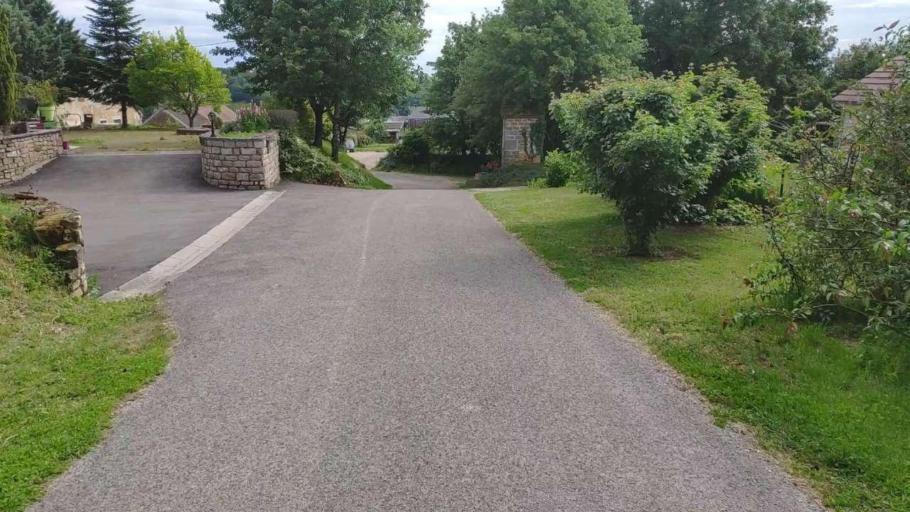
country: FR
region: Franche-Comte
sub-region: Departement du Jura
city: Bletterans
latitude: 46.7959
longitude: 5.5562
